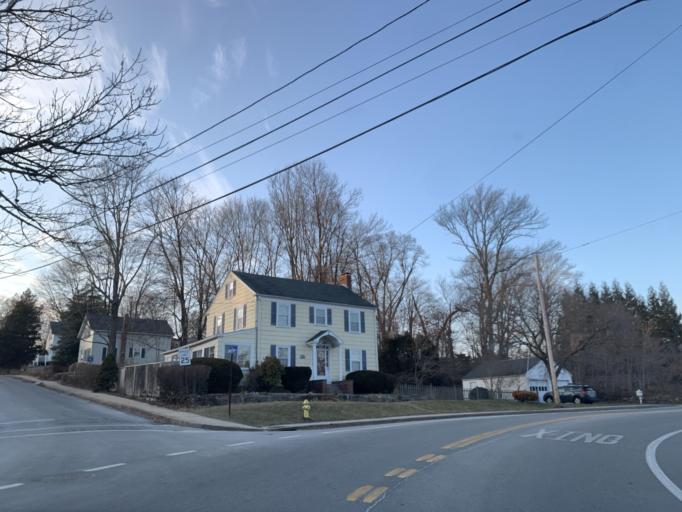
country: US
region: Rhode Island
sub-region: Washington County
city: Wakefield-Peacedale
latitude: 41.4519
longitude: -71.5018
